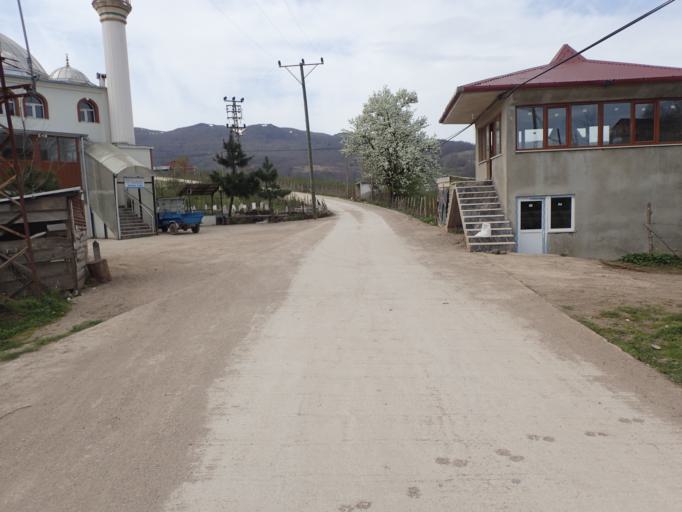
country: TR
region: Ordu
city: Aybasti
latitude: 40.6997
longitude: 37.2722
